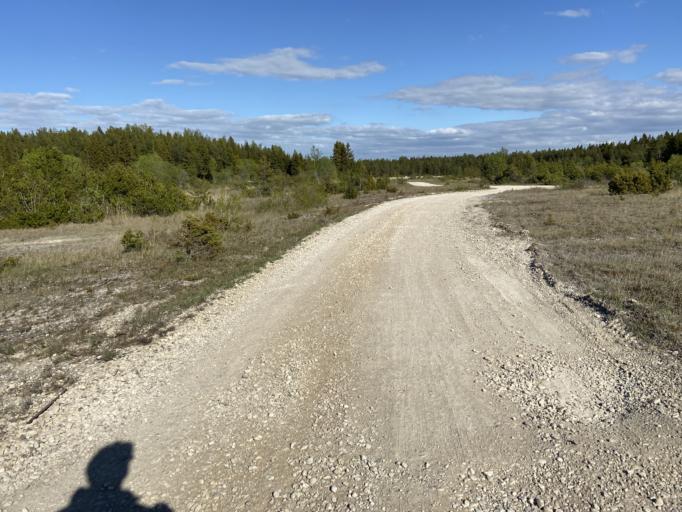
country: EE
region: Harju
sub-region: Paldiski linn
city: Paldiski
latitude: 59.2683
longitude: 23.7401
